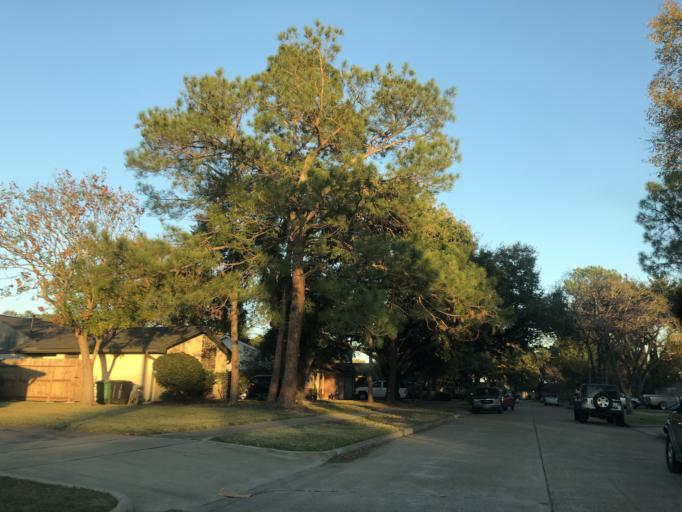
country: US
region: Texas
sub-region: Harris County
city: Bellaire
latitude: 29.6865
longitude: -95.5176
